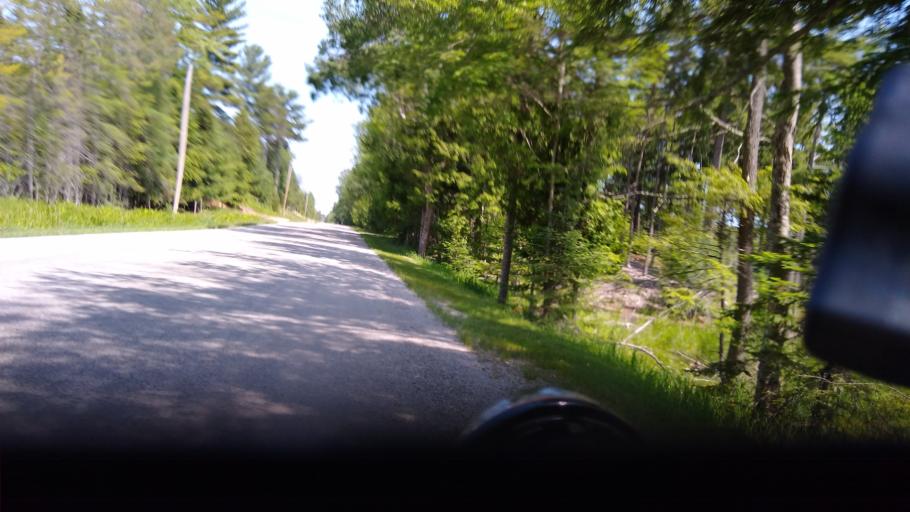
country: US
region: Michigan
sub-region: Delta County
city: Escanaba
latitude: 45.7100
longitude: -87.1554
